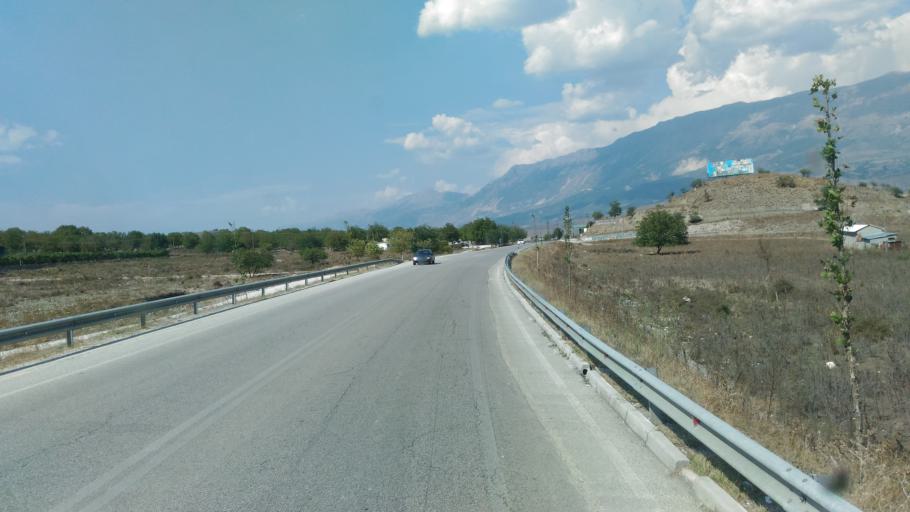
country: AL
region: Gjirokaster
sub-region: Rrethi i Gjirokastres
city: Dervician
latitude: 40.0419
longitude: 20.1759
